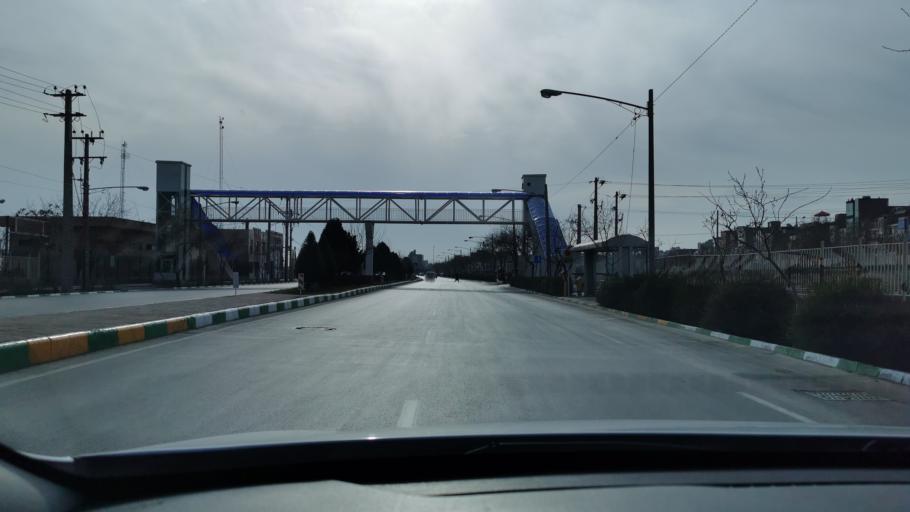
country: IR
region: Razavi Khorasan
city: Mashhad
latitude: 36.3015
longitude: 59.5189
